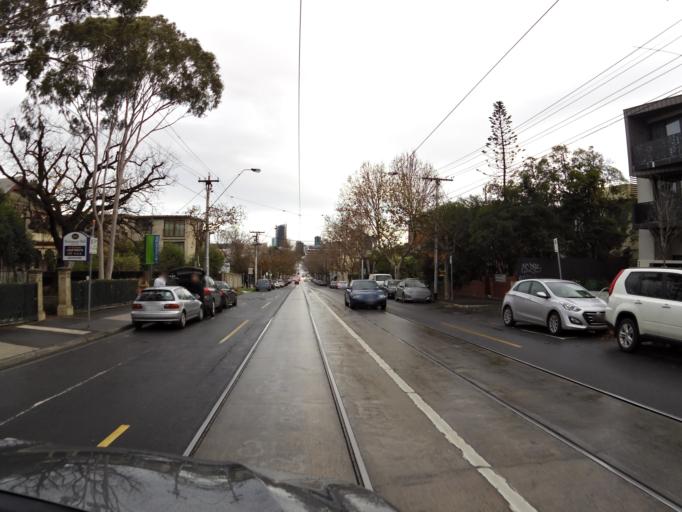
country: AU
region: Victoria
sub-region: Yarra
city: Richmond
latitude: -37.8228
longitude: 144.9985
